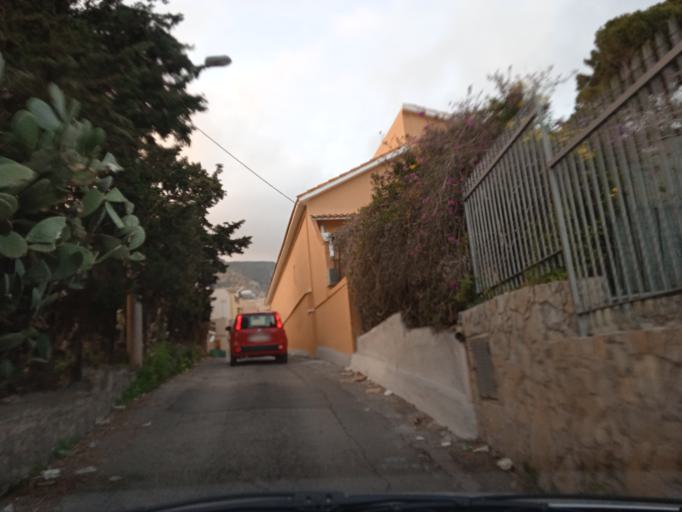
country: IT
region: Sicily
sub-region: Palermo
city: Santa Flavia
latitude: 38.0938
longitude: 13.5392
